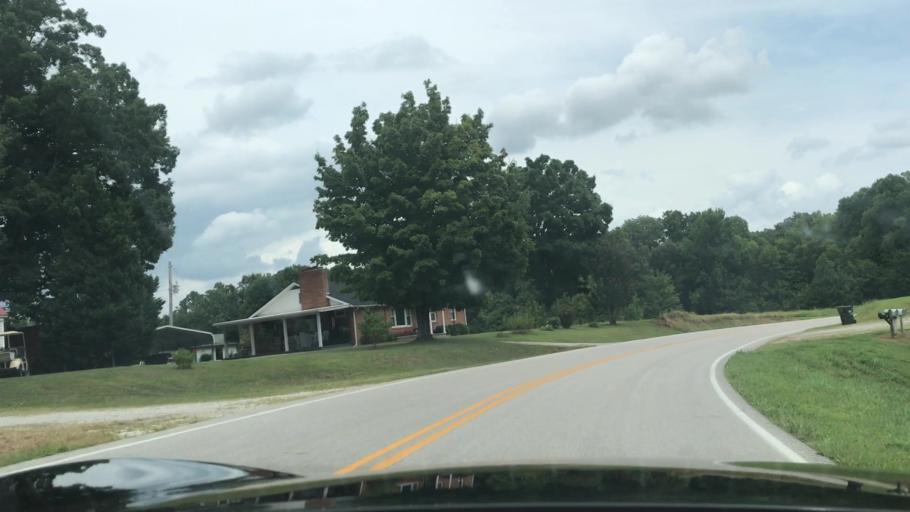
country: US
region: Kentucky
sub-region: Butler County
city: Morgantown
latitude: 37.1809
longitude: -86.8633
